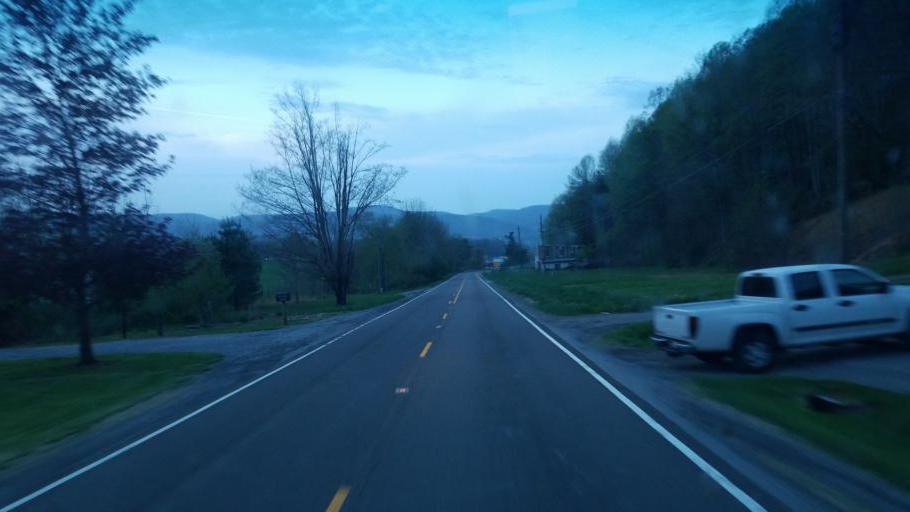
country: US
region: Virginia
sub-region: Smyth County
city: Atkins
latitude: 36.7955
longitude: -81.4017
